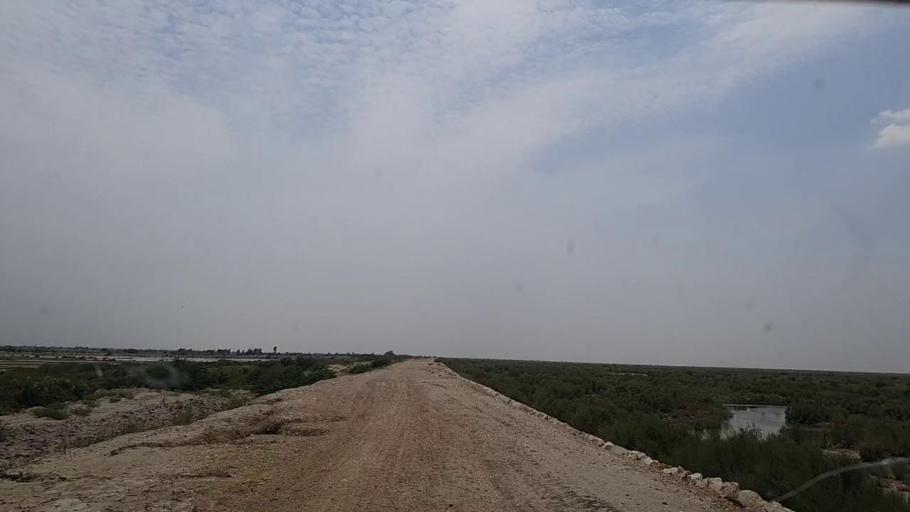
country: PK
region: Sindh
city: Phulji
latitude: 26.8652
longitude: 67.6428
